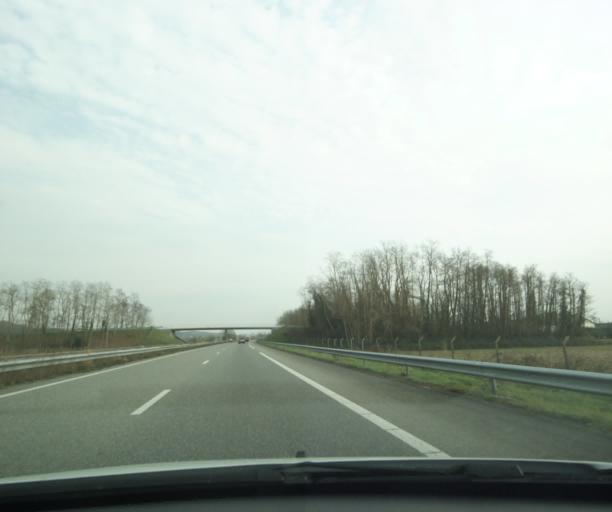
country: FR
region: Aquitaine
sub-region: Departement des Pyrenees-Atlantiques
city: Artix
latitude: 43.4120
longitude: -0.5681
